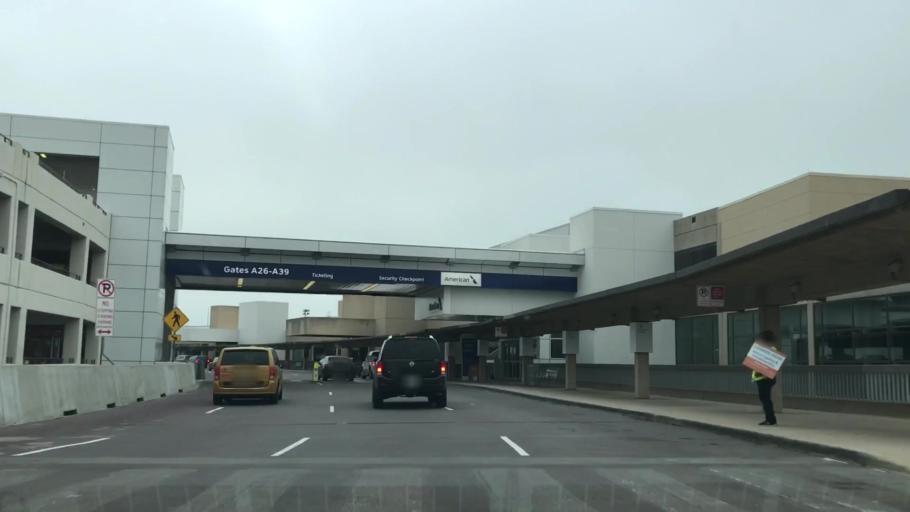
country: US
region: Texas
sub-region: Tarrant County
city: Grapevine
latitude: 32.9028
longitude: -97.0386
